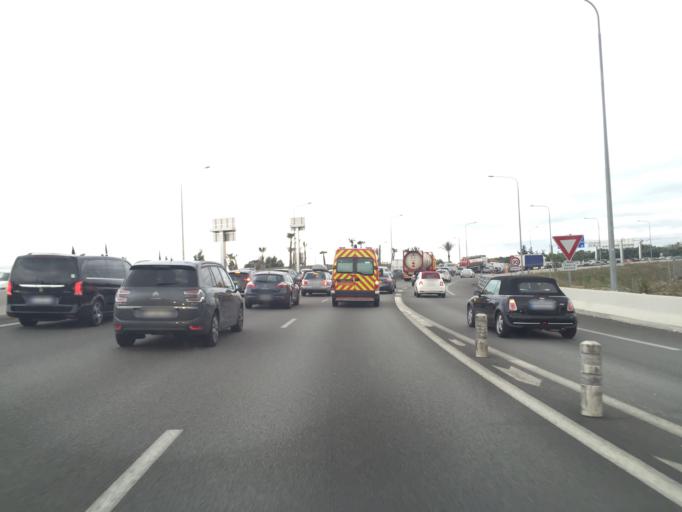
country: FR
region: Provence-Alpes-Cote d'Azur
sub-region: Departement des Alpes-Maritimes
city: Saint-Laurent-du-Var
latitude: 43.6707
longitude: 7.2015
